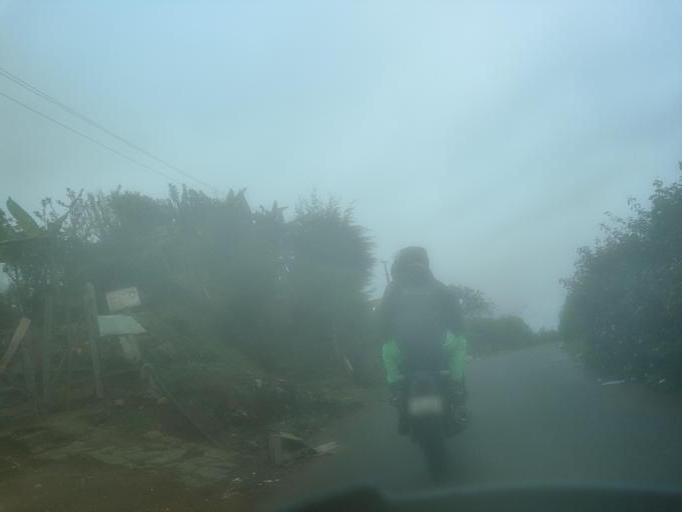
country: IN
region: Tamil Nadu
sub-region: Dindigul
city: Kodaikanal
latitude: 10.2050
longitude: 77.3414
